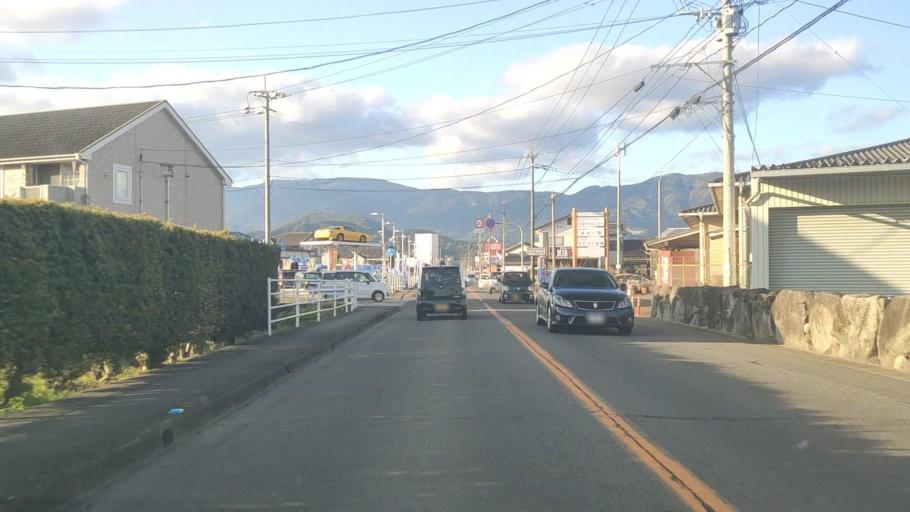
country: JP
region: Saga Prefecture
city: Saga-shi
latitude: 33.2849
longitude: 130.2090
